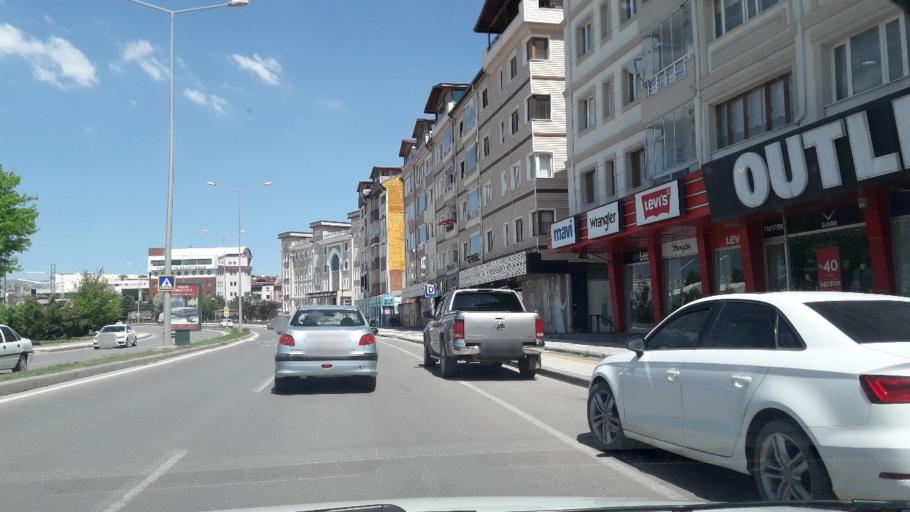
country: TR
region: Sivas
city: Sivas
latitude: 39.7403
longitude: 37.0153
